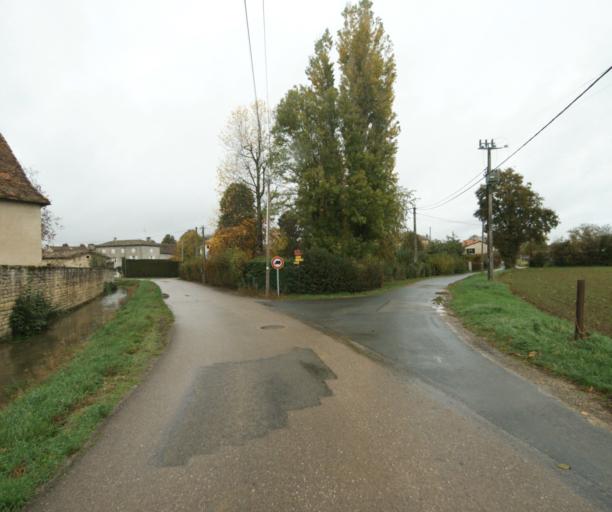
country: FR
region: Rhone-Alpes
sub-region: Departement de l'Ain
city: Pont-de-Vaux
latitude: 46.4813
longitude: 4.8681
